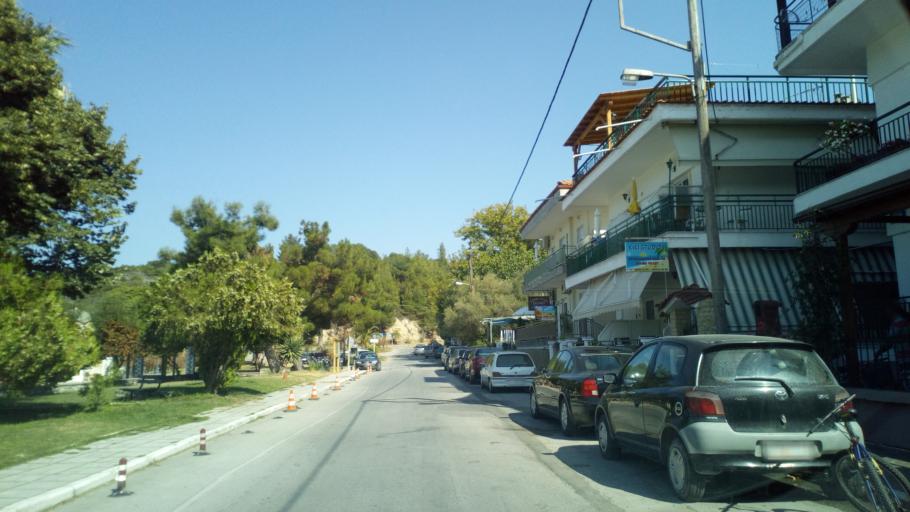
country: GR
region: Central Macedonia
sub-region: Nomos Chalkidikis
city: Stratonion
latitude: 40.5903
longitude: 23.7872
